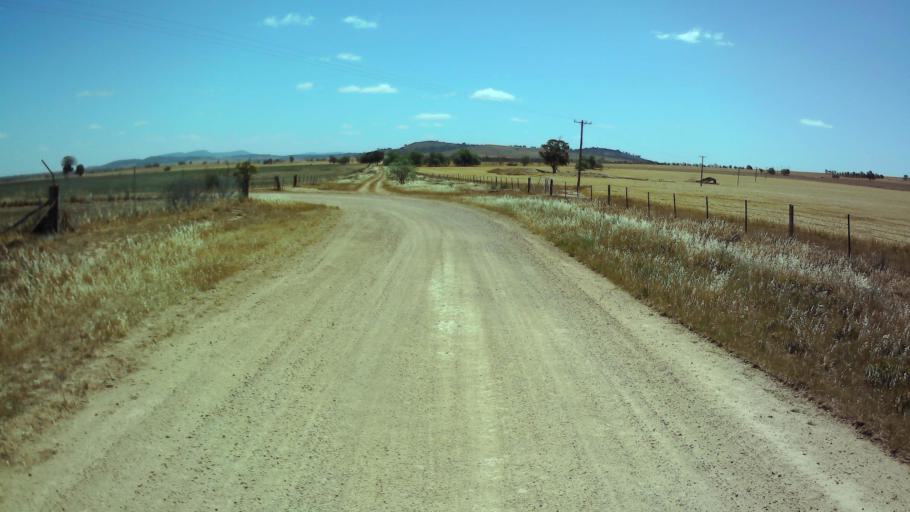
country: AU
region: New South Wales
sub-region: Weddin
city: Grenfell
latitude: -33.9712
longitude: 148.3283
